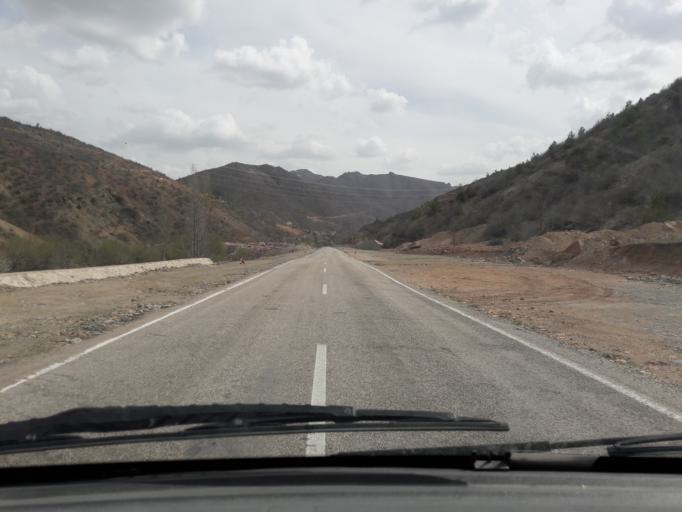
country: TR
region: Gumushane
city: Kale
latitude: 40.3816
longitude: 39.5777
